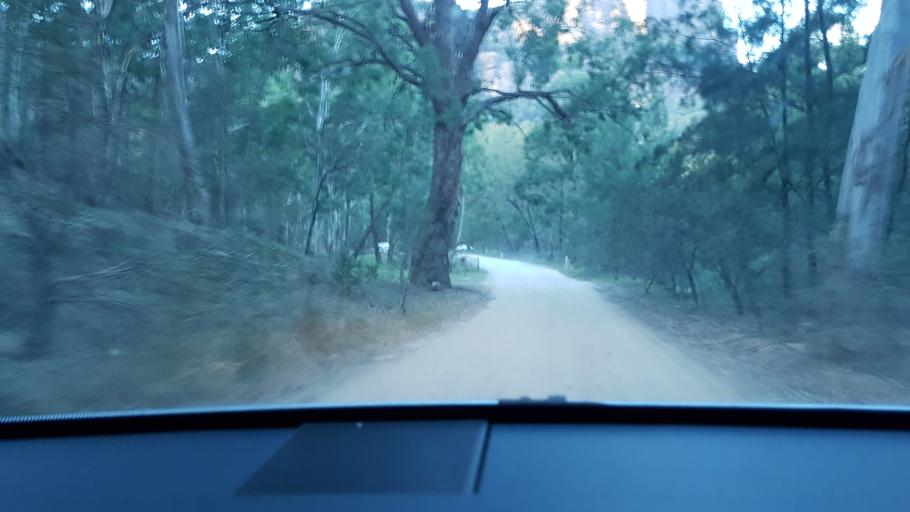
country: AU
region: New South Wales
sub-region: Lithgow
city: Portland
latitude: -33.1759
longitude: 150.2363
